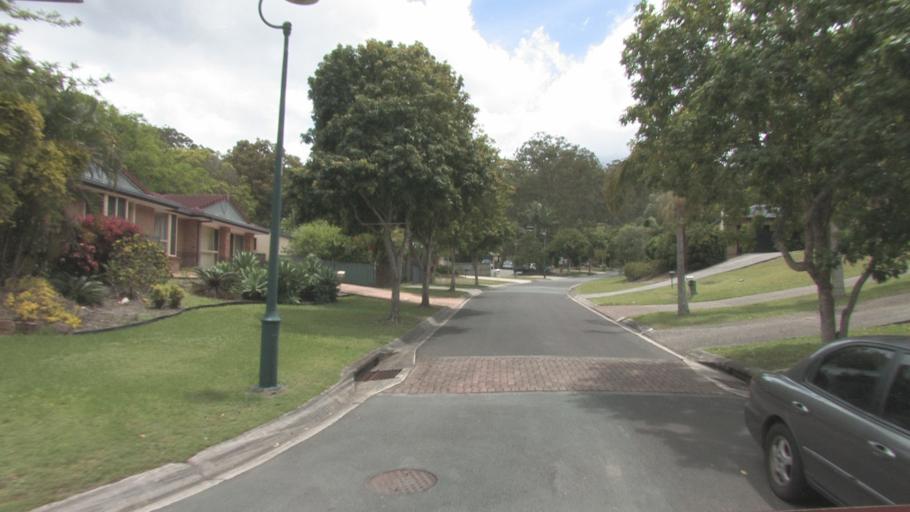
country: AU
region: Queensland
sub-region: Logan
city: Slacks Creek
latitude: -27.6499
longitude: 153.1861
